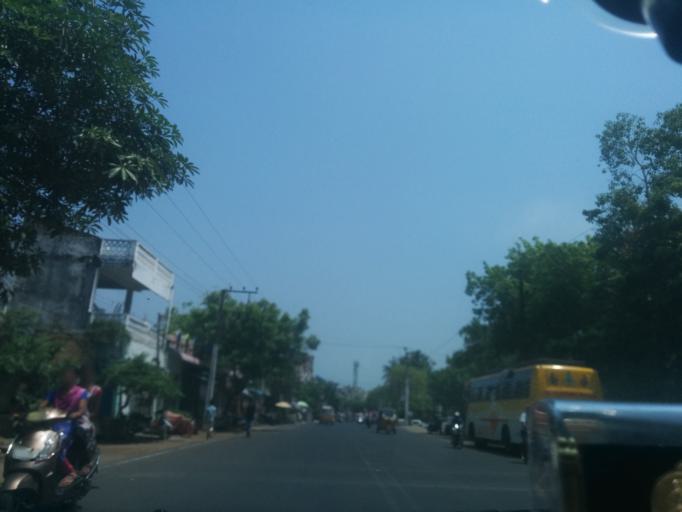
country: IN
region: Andhra Pradesh
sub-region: East Godavari
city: Rajahmundry
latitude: 17.0142
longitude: 81.7721
